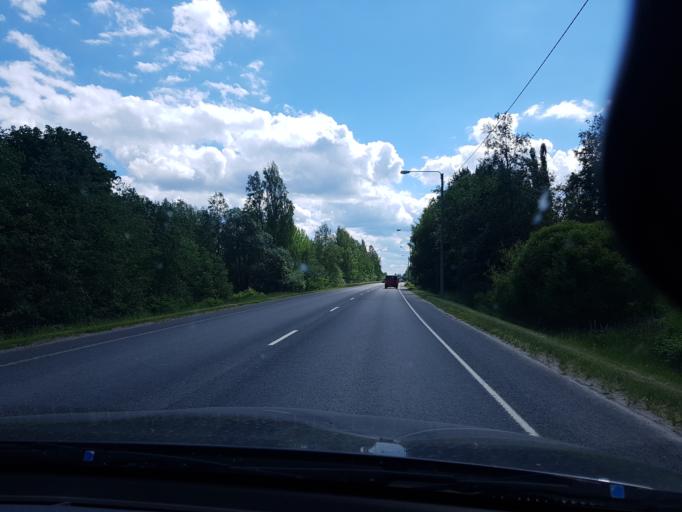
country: FI
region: Haeme
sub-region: Haemeenlinna
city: Parola
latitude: 61.0663
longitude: 24.3925
